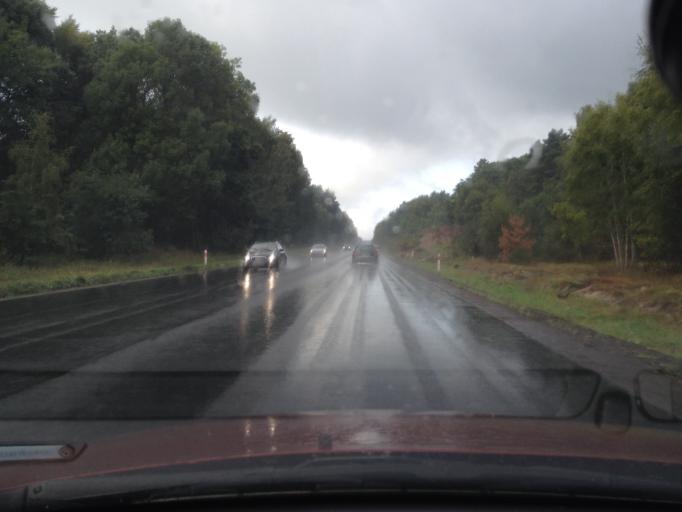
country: PL
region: West Pomeranian Voivodeship
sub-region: Powiat gryficki
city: Pobierowo
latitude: 54.0468
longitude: 14.9184
